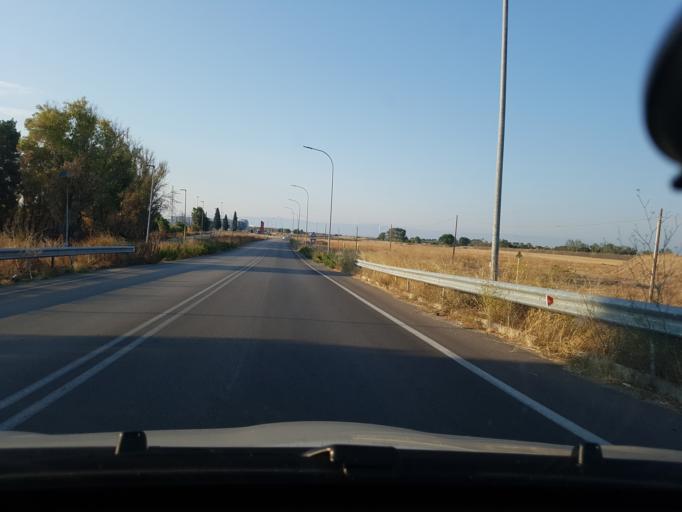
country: IT
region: Apulia
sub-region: Provincia di Foggia
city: Carapelle
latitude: 41.4089
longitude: 15.6532
